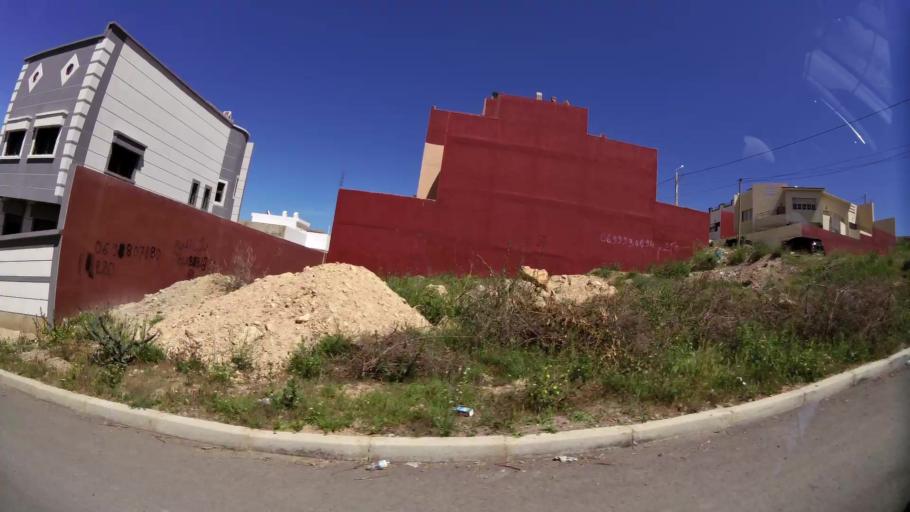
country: MA
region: Oriental
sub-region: Oujda-Angad
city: Oujda
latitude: 34.6463
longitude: -1.9055
